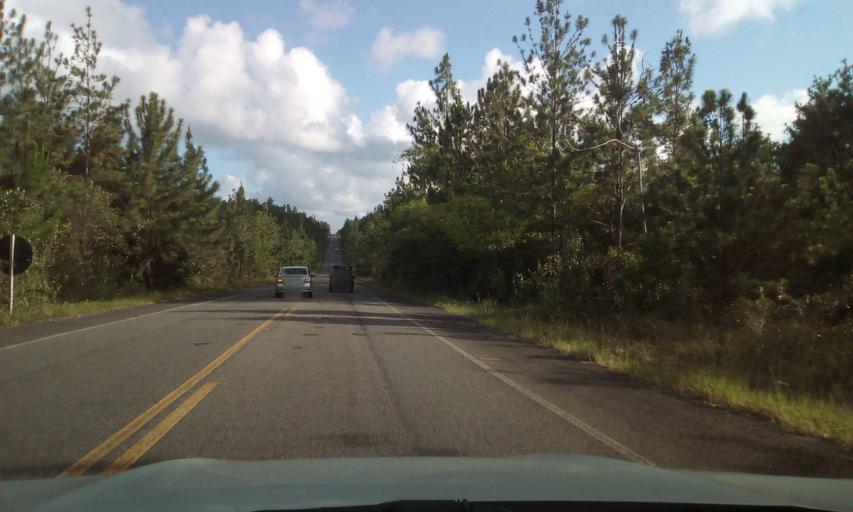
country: BR
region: Bahia
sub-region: Entre Rios
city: Entre Rios
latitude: -12.1289
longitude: -37.7914
